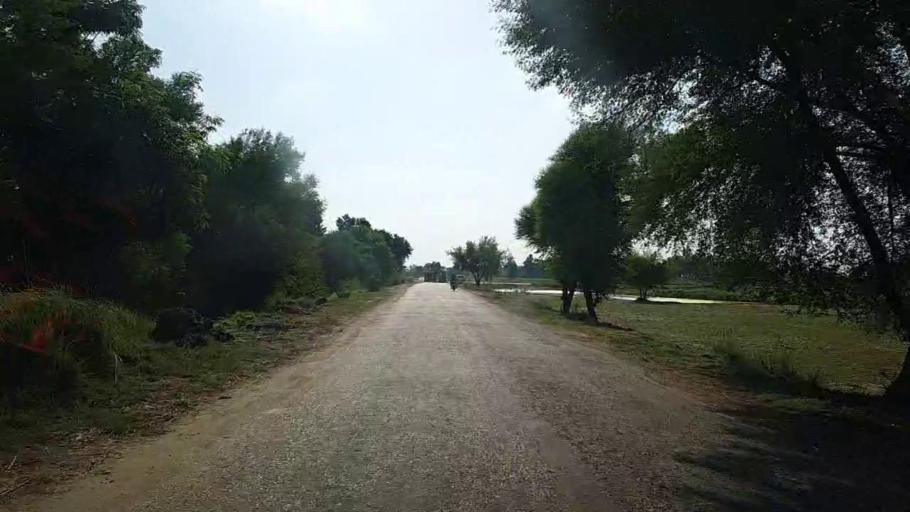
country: PK
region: Sindh
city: Kandiaro
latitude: 27.0561
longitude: 68.3193
